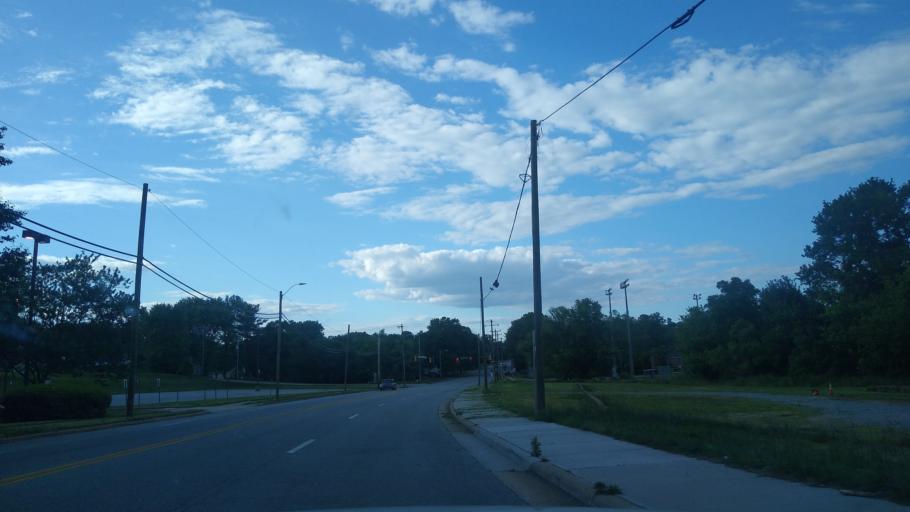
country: US
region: North Carolina
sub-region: Guilford County
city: Greensboro
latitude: 36.1003
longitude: -79.7751
